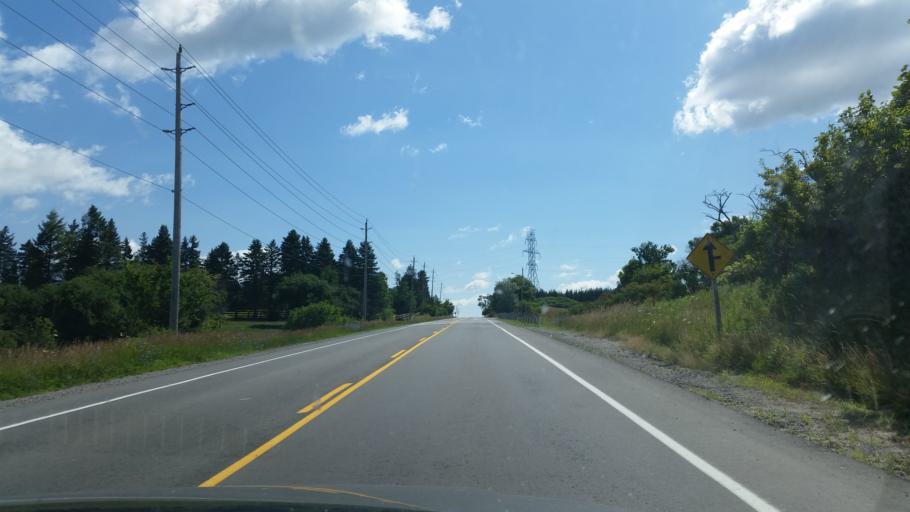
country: CA
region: Ontario
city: Vaughan
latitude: 43.9091
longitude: -79.6195
